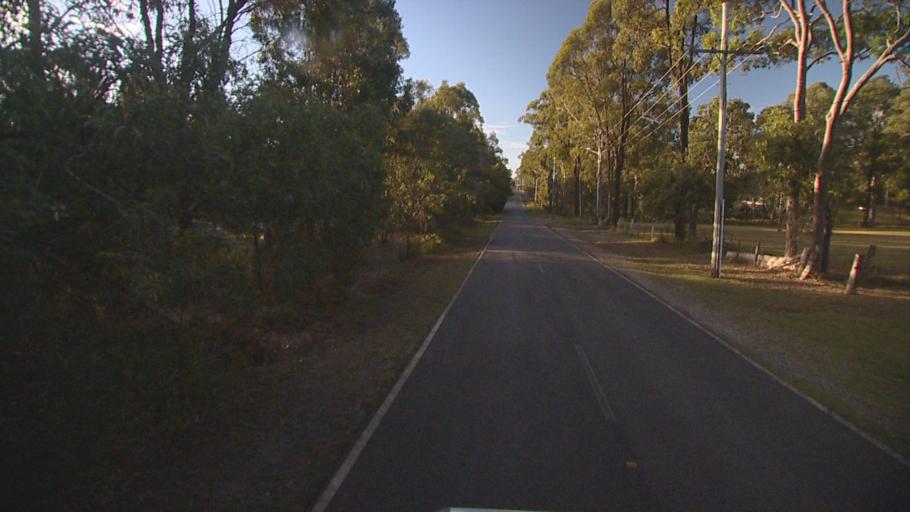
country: AU
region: Queensland
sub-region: Logan
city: Waterford West
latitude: -27.7256
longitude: 153.1413
